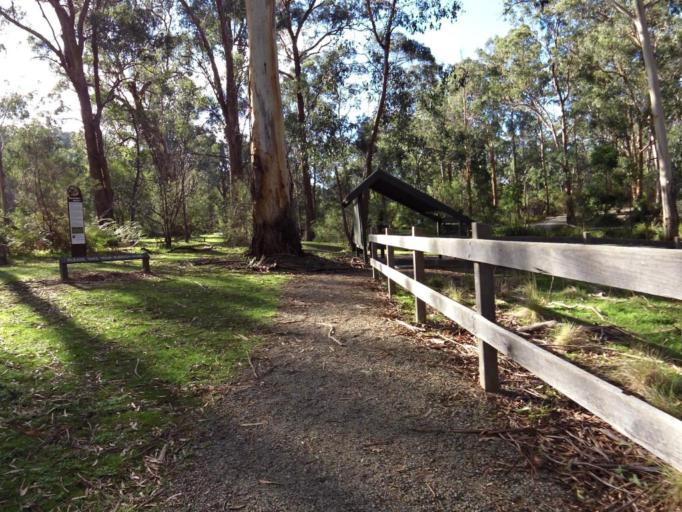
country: AU
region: Victoria
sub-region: Nillumbik
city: North Warrandyte
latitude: -37.7370
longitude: 145.1989
